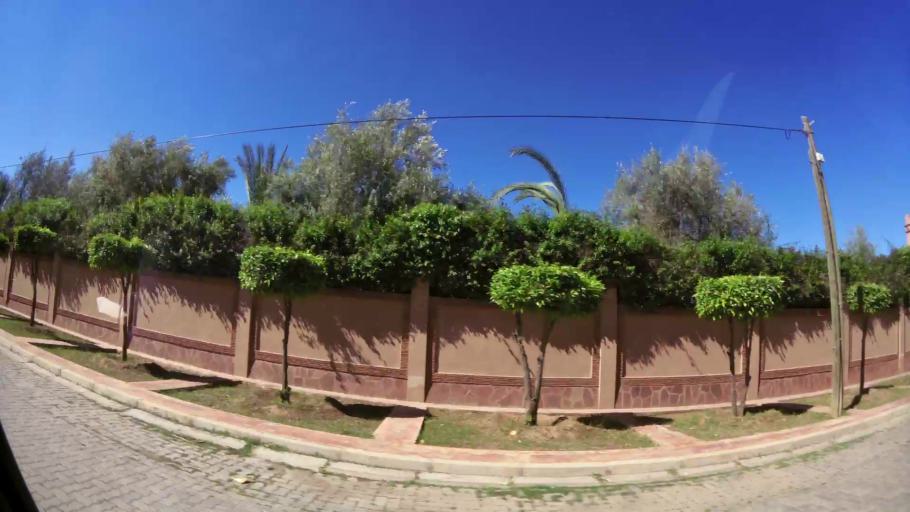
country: MA
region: Marrakech-Tensift-Al Haouz
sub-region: Marrakech
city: Marrakesh
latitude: 31.6520
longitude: -7.9700
